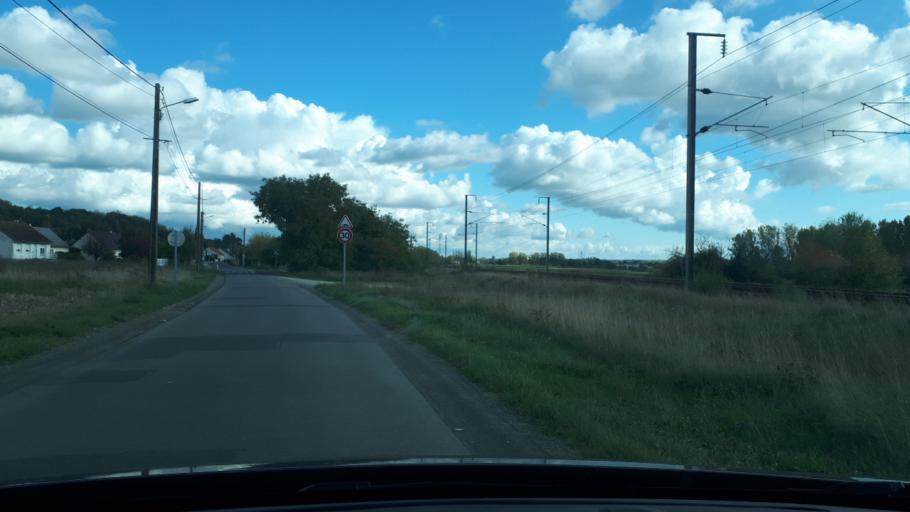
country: FR
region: Centre
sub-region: Departement du Loir-et-Cher
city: Saint-Aignan
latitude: 47.2931
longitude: 1.3703
